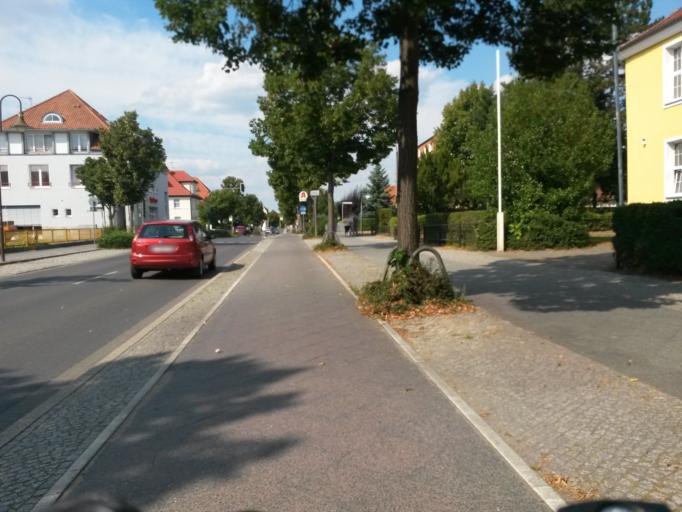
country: DE
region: Brandenburg
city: Templin
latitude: 53.1153
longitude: 13.5117
